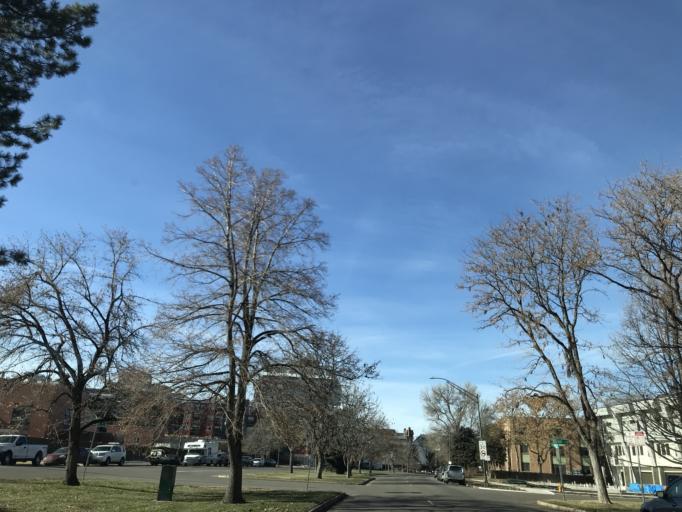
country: US
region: Colorado
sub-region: Arapahoe County
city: Glendale
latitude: 39.7338
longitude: -104.9356
